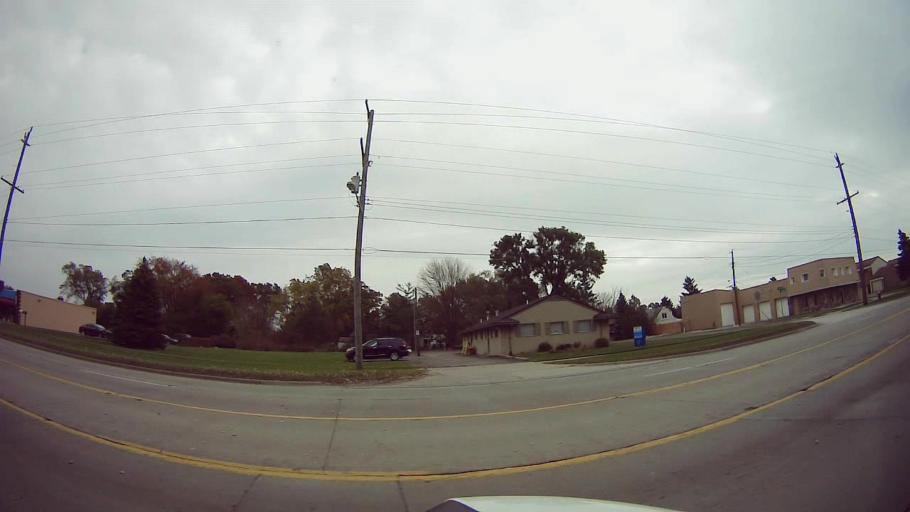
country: US
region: Michigan
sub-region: Oakland County
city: Madison Heights
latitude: 42.5098
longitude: -83.0859
